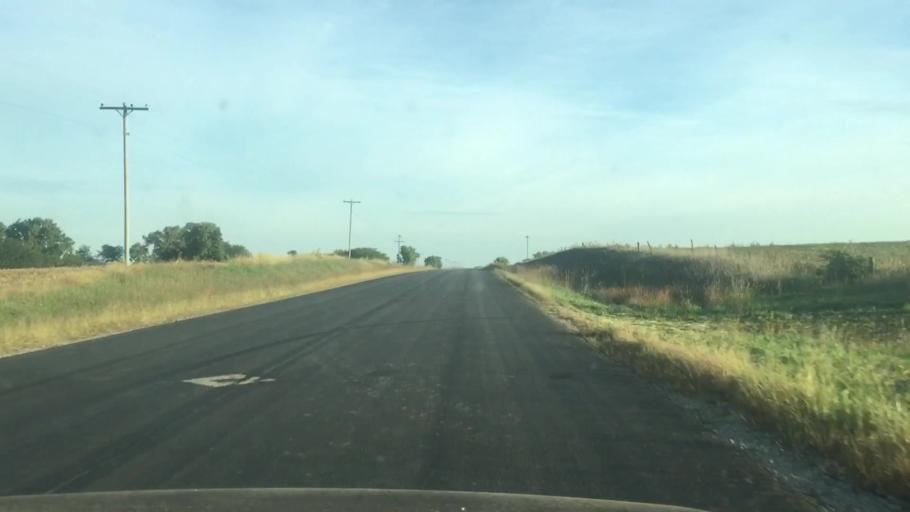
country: US
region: Kansas
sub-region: Marshall County
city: Marysville
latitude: 39.8782
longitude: -96.6009
